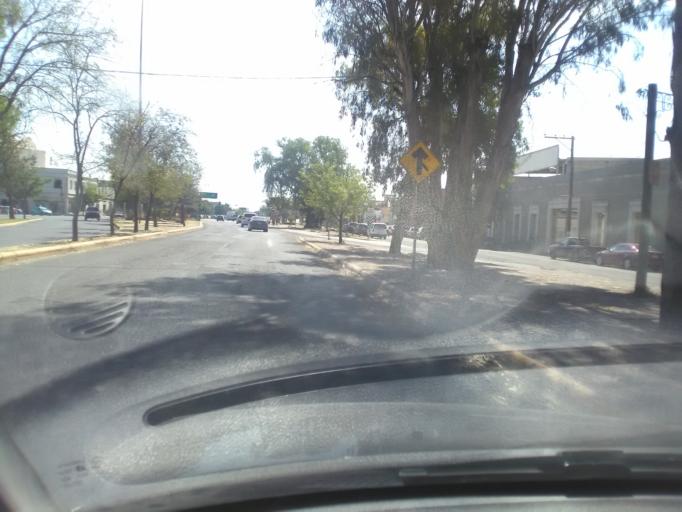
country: MX
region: Durango
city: Victoria de Durango
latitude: 24.0200
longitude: -104.6690
